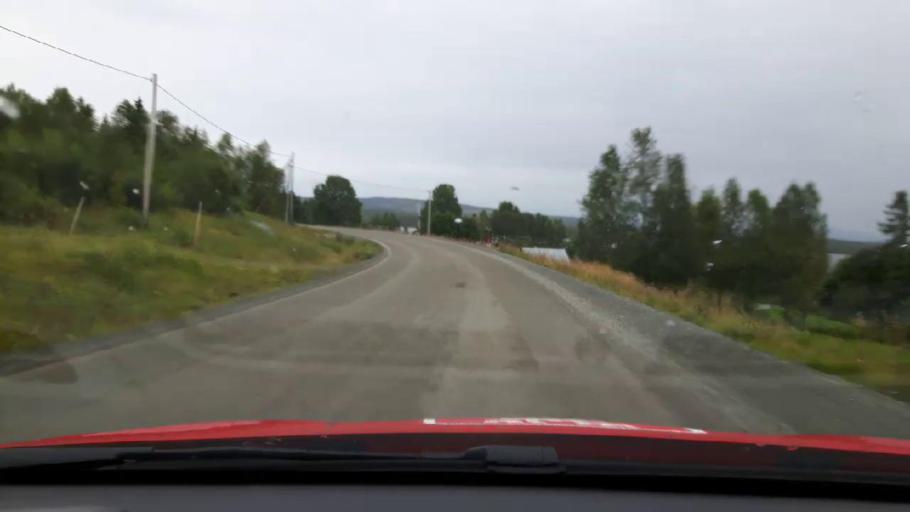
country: SE
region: Jaemtland
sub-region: Are Kommun
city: Are
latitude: 63.4599
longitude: 12.6362
